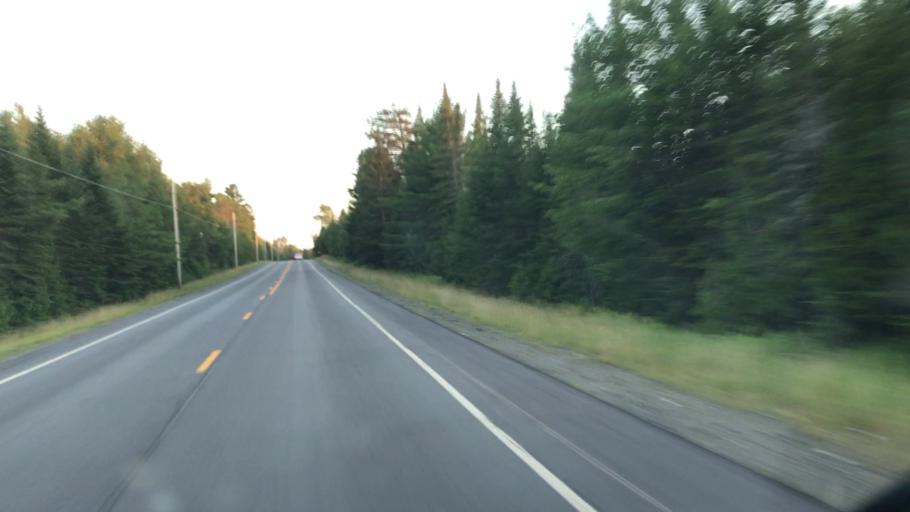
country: US
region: Maine
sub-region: Penobscot County
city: Medway
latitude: 45.5718
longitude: -68.3210
